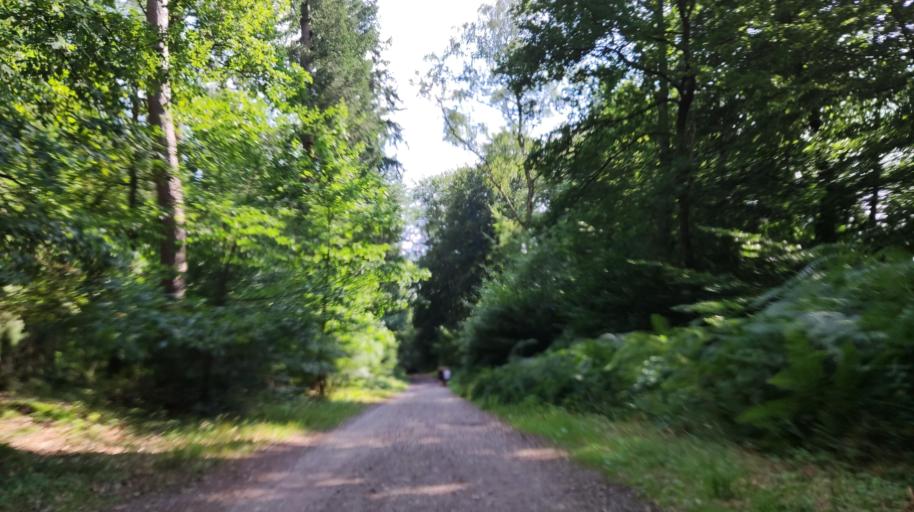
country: DE
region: Lower Saxony
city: Deutsch Evern
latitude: 53.2216
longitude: 10.4237
